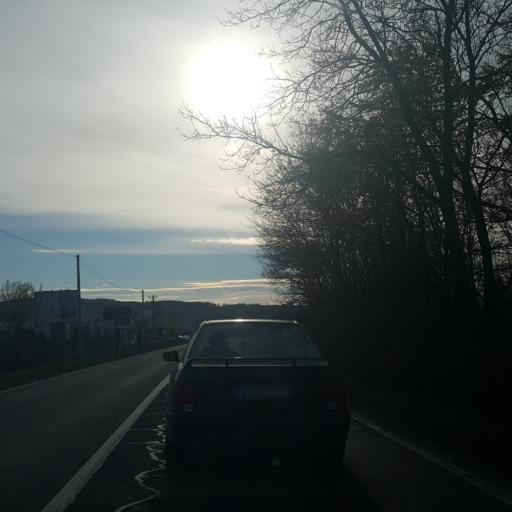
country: RS
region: Central Serbia
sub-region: Belgrade
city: Lazarevac
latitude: 44.3846
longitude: 20.2349
